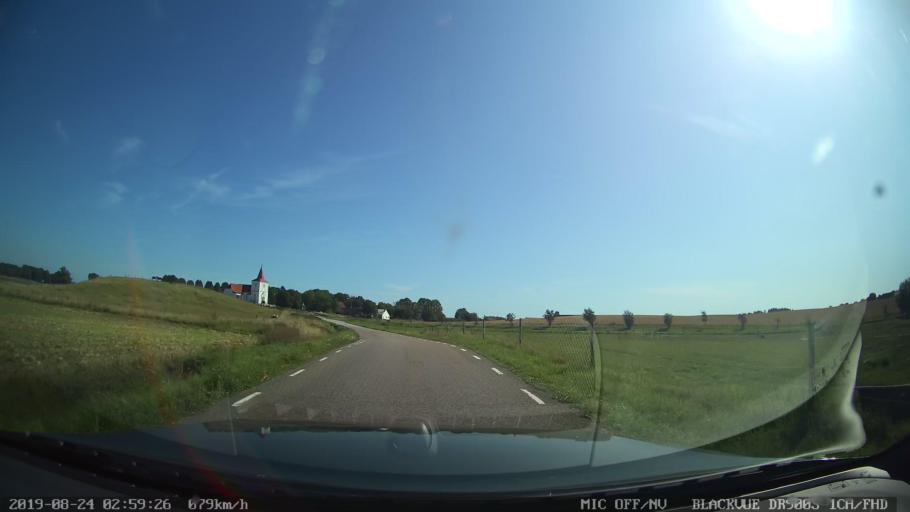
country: SE
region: Skane
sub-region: Skurups Kommun
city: Skurup
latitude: 55.4661
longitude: 13.4272
